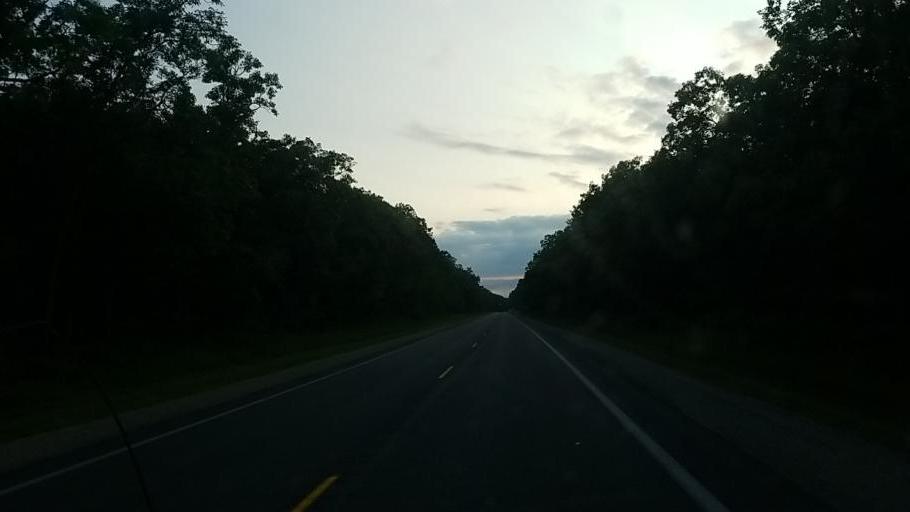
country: US
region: Michigan
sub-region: Newaygo County
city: Newaygo
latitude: 43.4056
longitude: -85.7509
